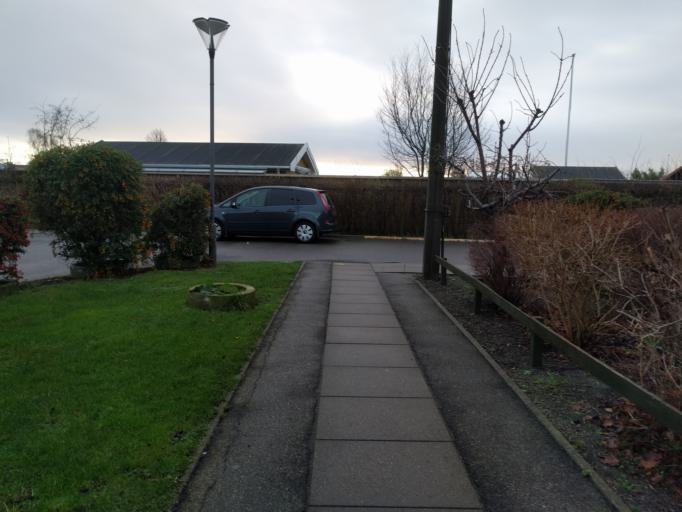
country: DK
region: Capital Region
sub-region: Tarnby Kommune
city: Tarnby
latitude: 55.6448
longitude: 12.6364
